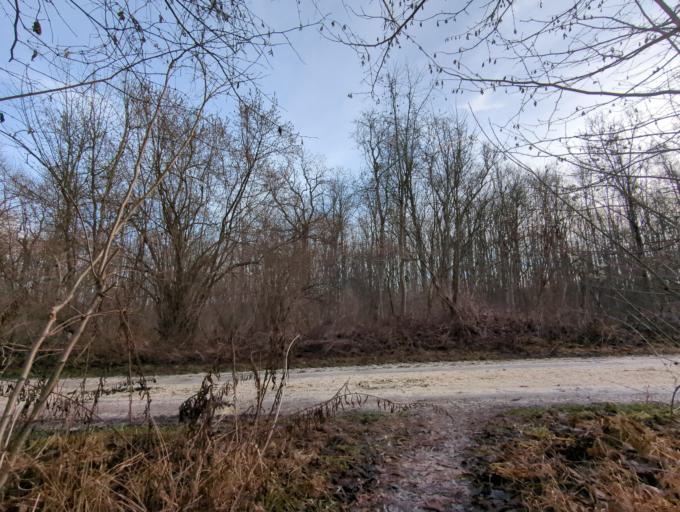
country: DE
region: Bavaria
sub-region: Swabia
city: Leipheim
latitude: 48.4455
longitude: 10.1744
